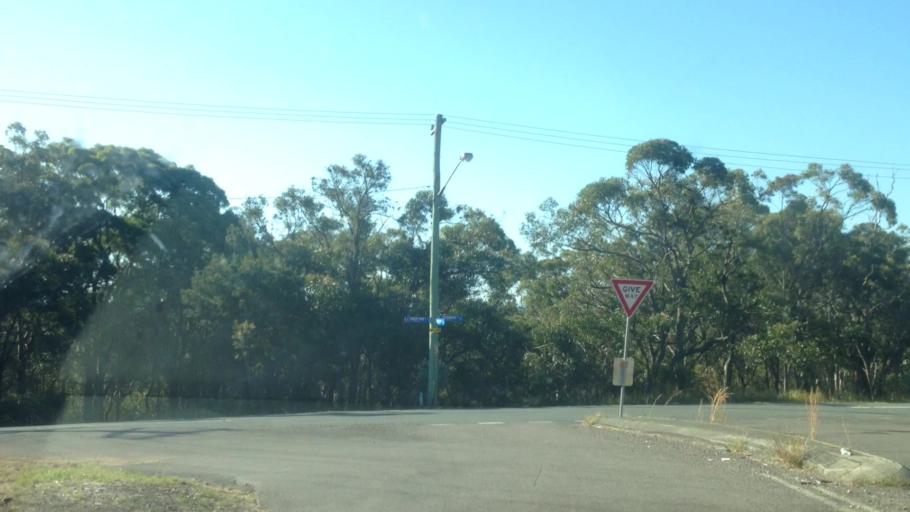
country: AU
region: New South Wales
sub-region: Lake Macquarie Shire
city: Arcadia vale
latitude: -33.1078
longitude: 151.5589
